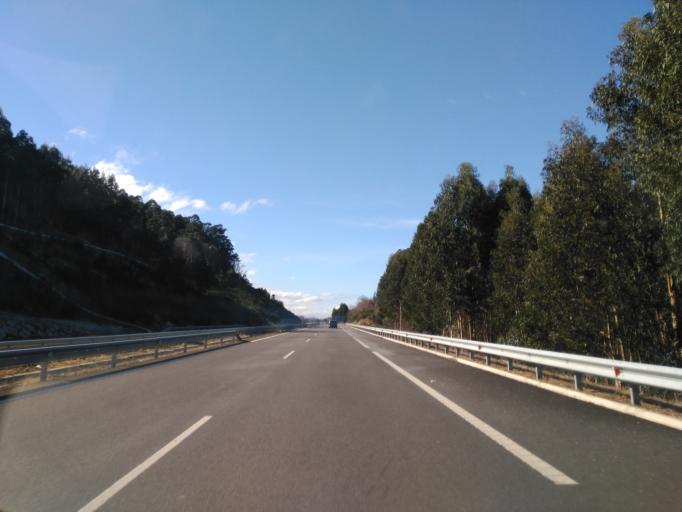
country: ES
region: Asturias
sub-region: Province of Asturias
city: Llanes
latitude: 43.3924
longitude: -4.6317
